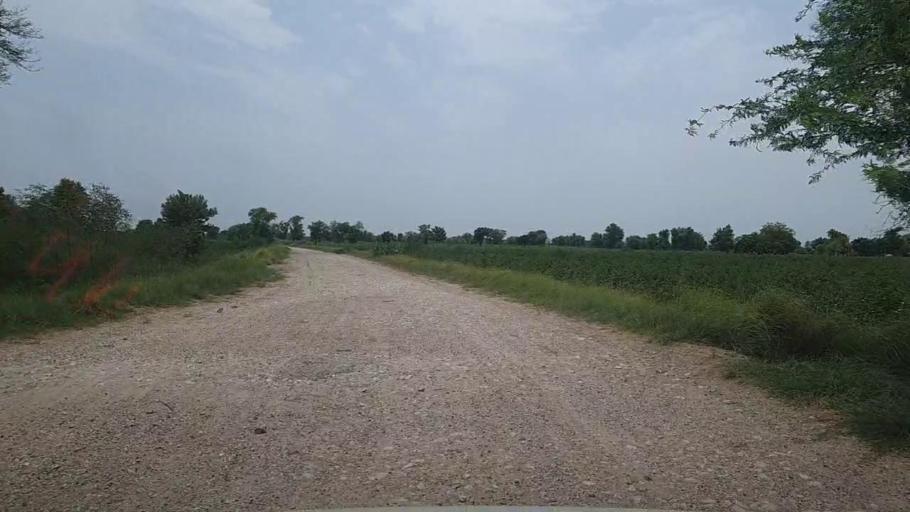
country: PK
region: Sindh
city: Karaundi
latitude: 26.9166
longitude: 68.3268
